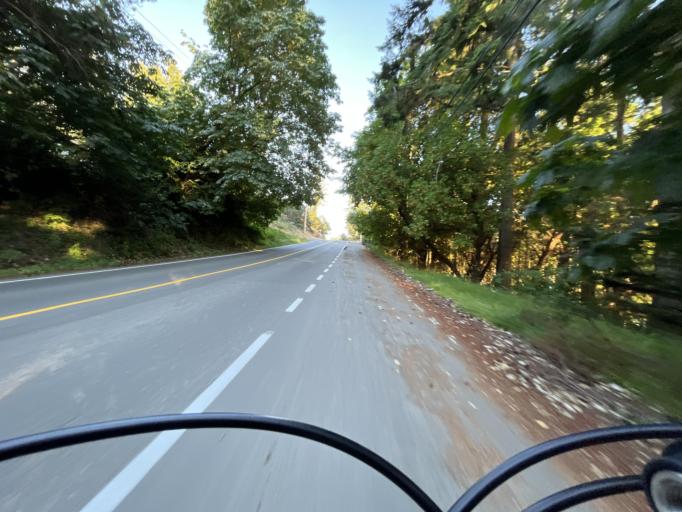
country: CA
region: British Columbia
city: Langford
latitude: 48.4521
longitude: -123.5287
